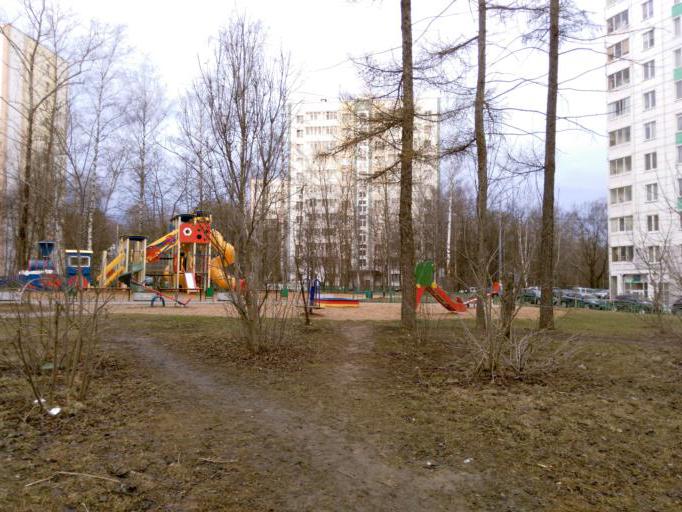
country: RU
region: Moscow
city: Zelenograd
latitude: 55.9988
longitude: 37.2018
